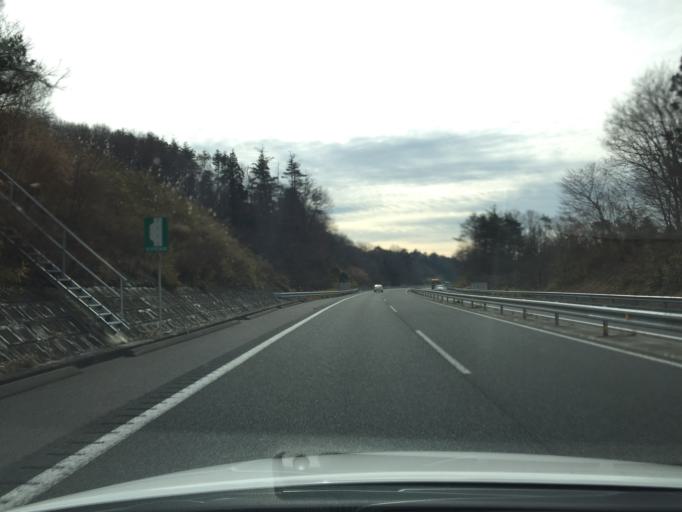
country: JP
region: Fukushima
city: Funehikimachi-funehiki
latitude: 37.3304
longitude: 140.6168
